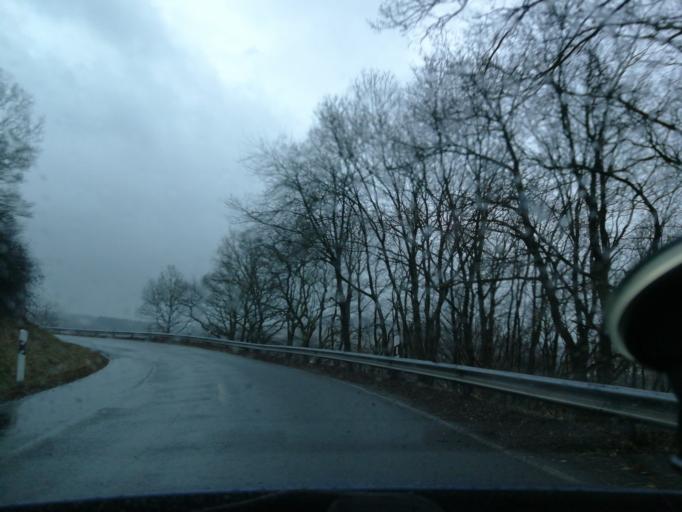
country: DE
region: Rheinland-Pfalz
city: Berglicht
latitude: 49.7919
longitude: 6.9645
